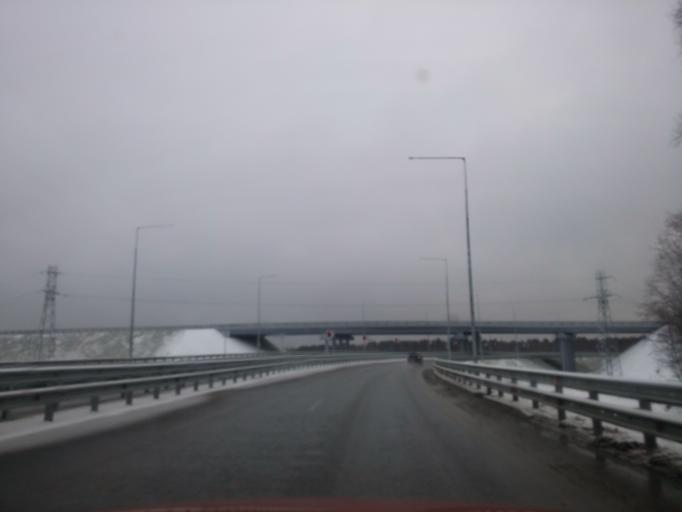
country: RU
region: Tverskaya
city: Likhoslavl'
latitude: 56.9523
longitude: 35.5131
